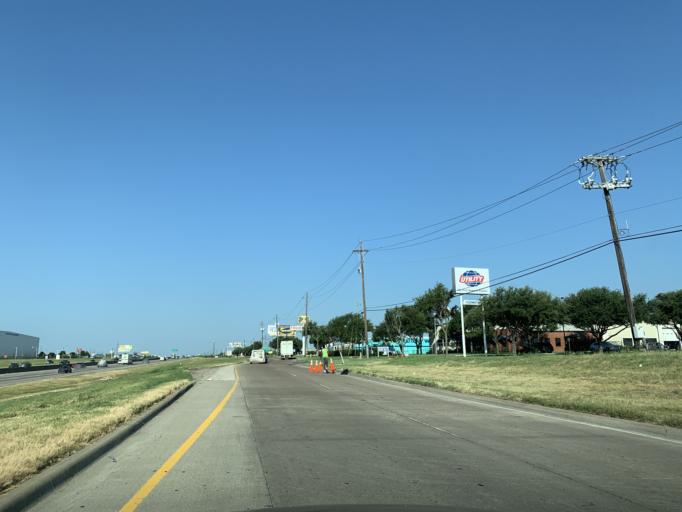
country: US
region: Texas
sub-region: Dallas County
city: Hutchins
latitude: 32.6554
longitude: -96.7521
